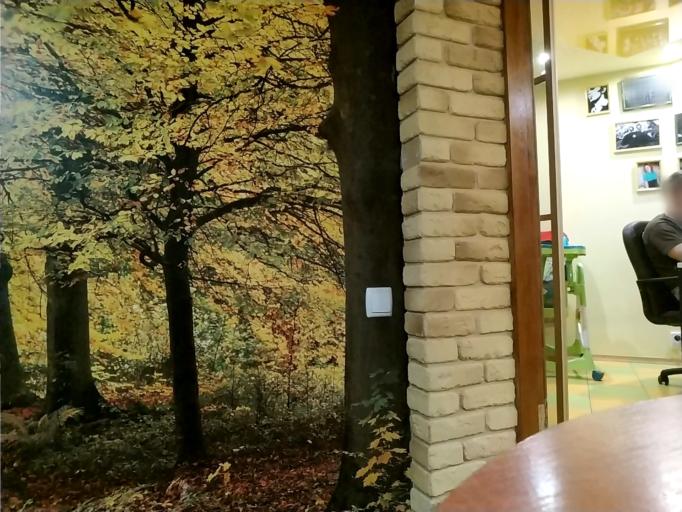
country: RU
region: Tverskaya
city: Zapadnaya Dvina
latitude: 56.3217
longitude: 31.9220
